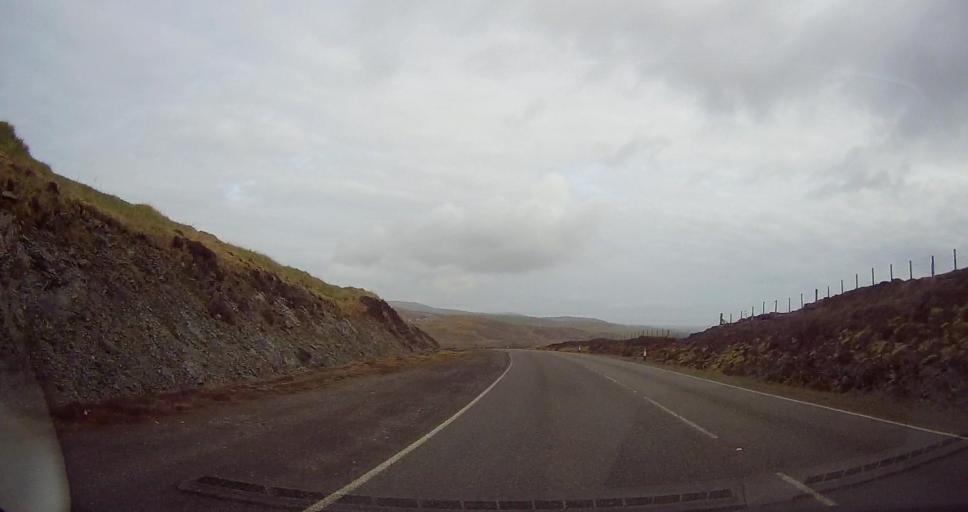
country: GB
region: Scotland
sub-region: Shetland Islands
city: Sandwick
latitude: 60.0885
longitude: -1.2297
